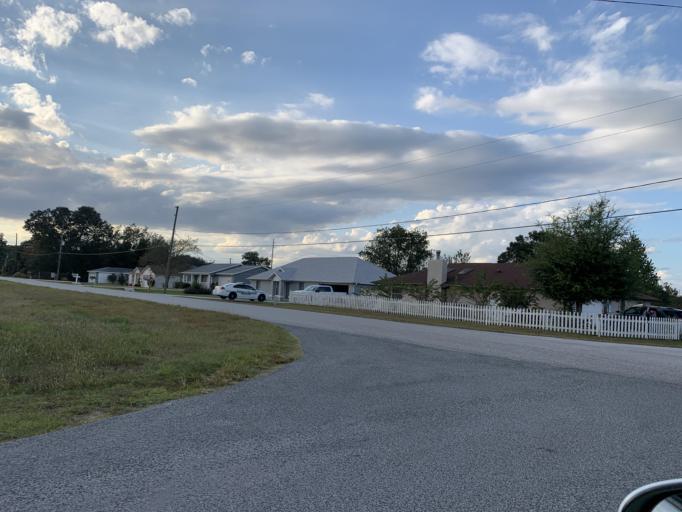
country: US
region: Florida
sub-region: Marion County
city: Silver Springs Shores
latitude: 29.1663
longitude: -82.0516
